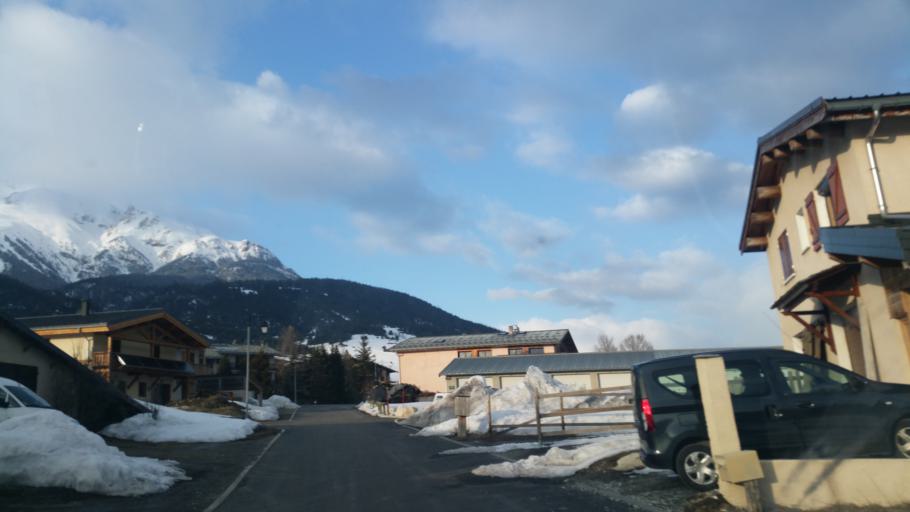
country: FR
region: Rhone-Alpes
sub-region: Departement de la Savoie
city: Modane
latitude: 45.2254
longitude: 6.7437
